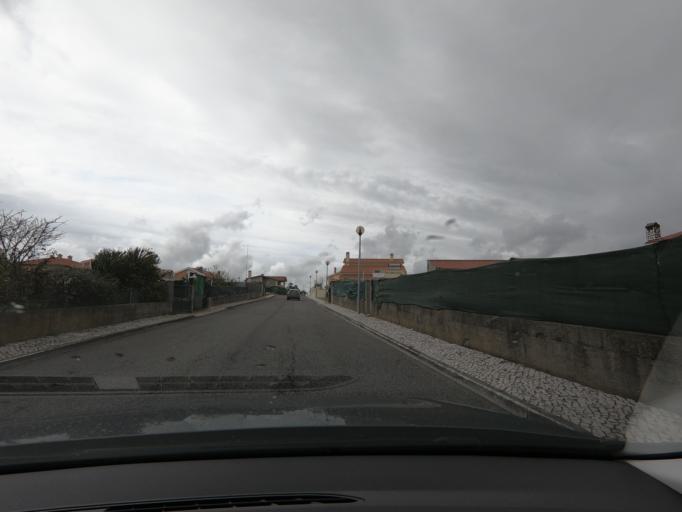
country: PT
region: Lisbon
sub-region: Cascais
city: Sao Domingos de Rana
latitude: 38.7322
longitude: -9.3316
